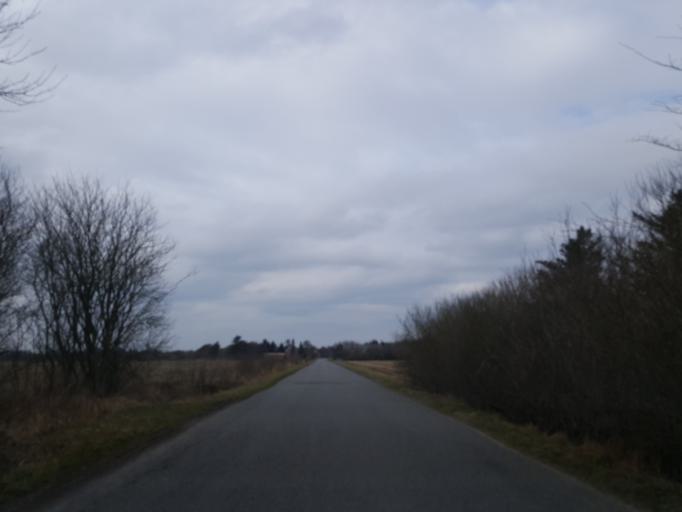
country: DK
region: Central Jutland
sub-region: Holstebro Kommune
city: Ulfborg
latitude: 56.3606
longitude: 8.2594
